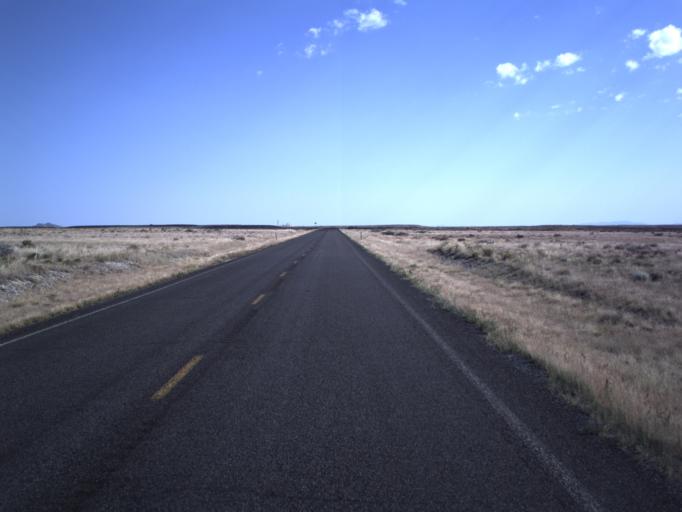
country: US
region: Utah
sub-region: Beaver County
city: Milford
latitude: 38.8791
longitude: -112.8325
